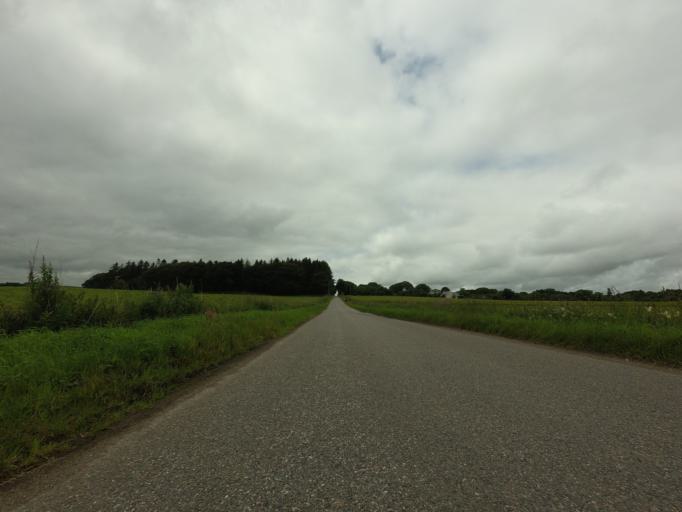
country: GB
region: Scotland
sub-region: Aberdeenshire
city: Mintlaw
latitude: 57.5292
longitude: -2.1477
